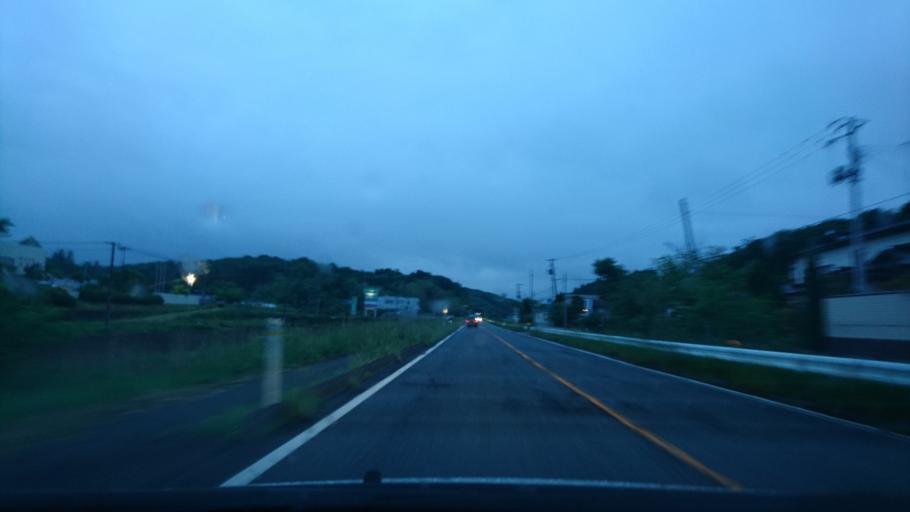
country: JP
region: Iwate
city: Ichinoseki
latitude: 38.7910
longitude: 141.0510
